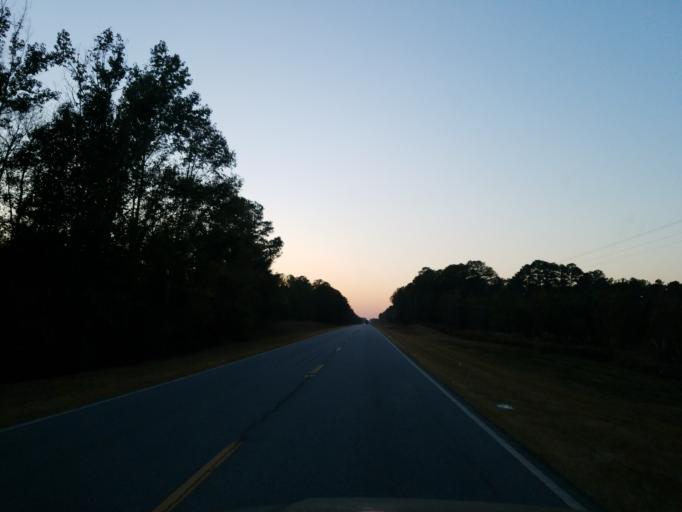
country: US
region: Georgia
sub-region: Turner County
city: Ashburn
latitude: 31.7213
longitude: -83.4785
